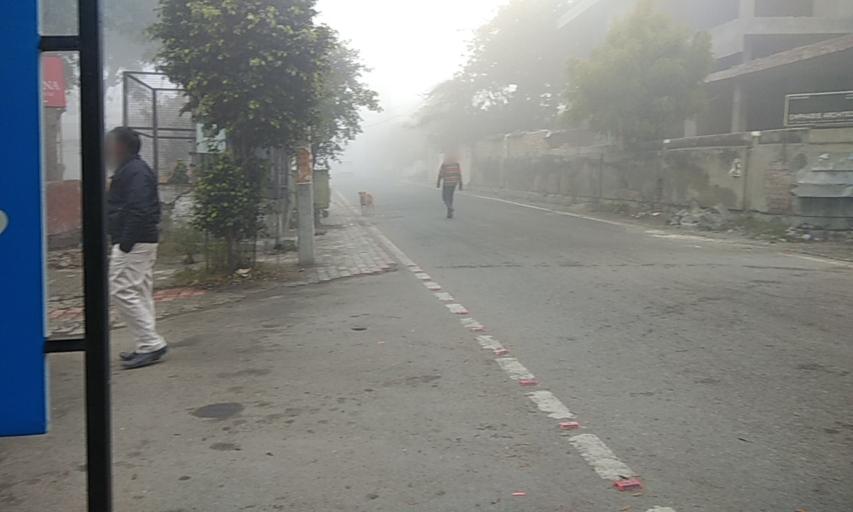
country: IN
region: Punjab
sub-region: Amritsar
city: Amritsar
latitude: 31.6448
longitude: 74.8658
